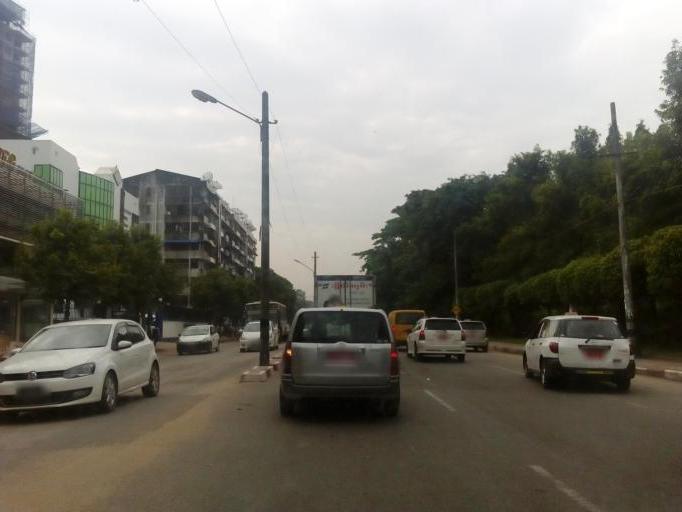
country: MM
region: Yangon
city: Yangon
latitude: 16.8439
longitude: 96.1261
